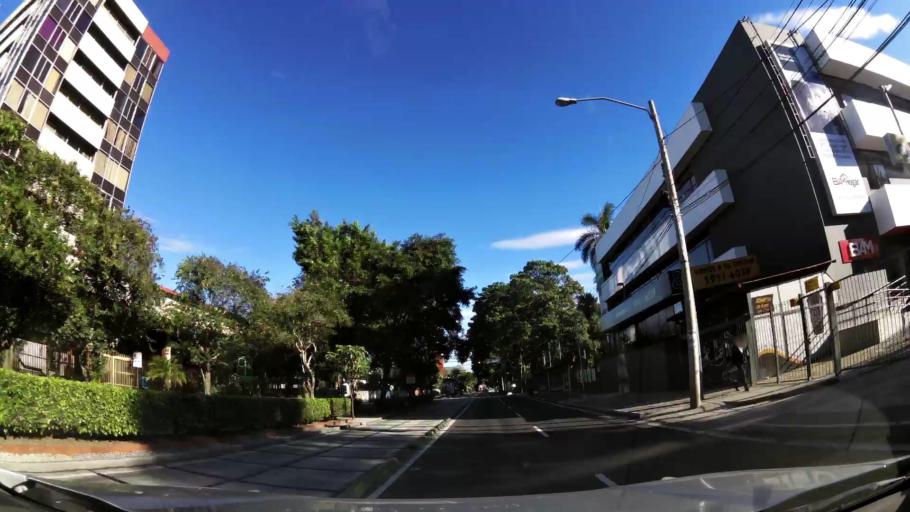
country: GT
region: Guatemala
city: Guatemala City
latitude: 14.6084
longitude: -90.5175
